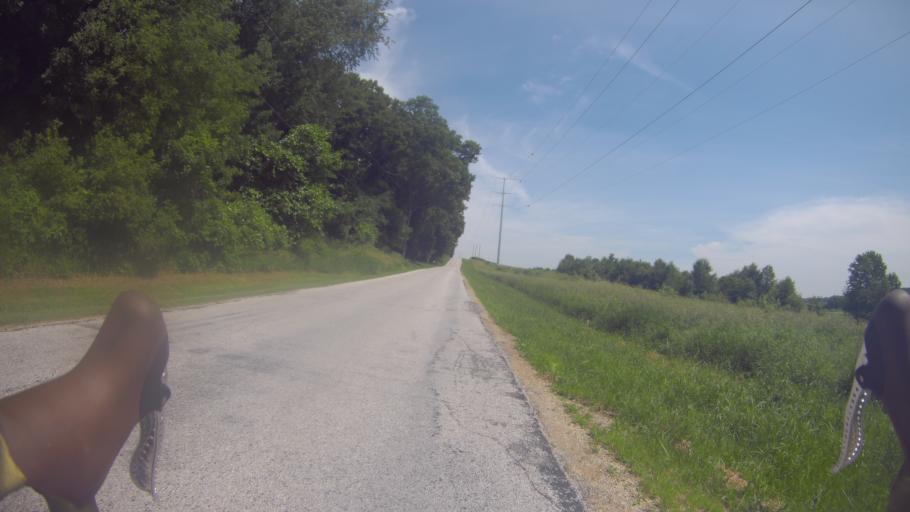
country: US
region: Wisconsin
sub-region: Dane County
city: Deerfield
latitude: 43.0503
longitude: -89.0412
